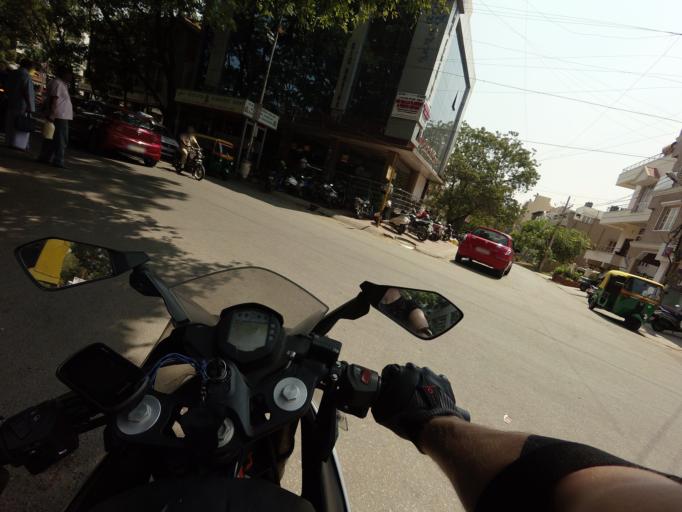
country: IN
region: Karnataka
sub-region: Bangalore Urban
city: Bangalore
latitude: 13.0022
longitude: 77.6613
